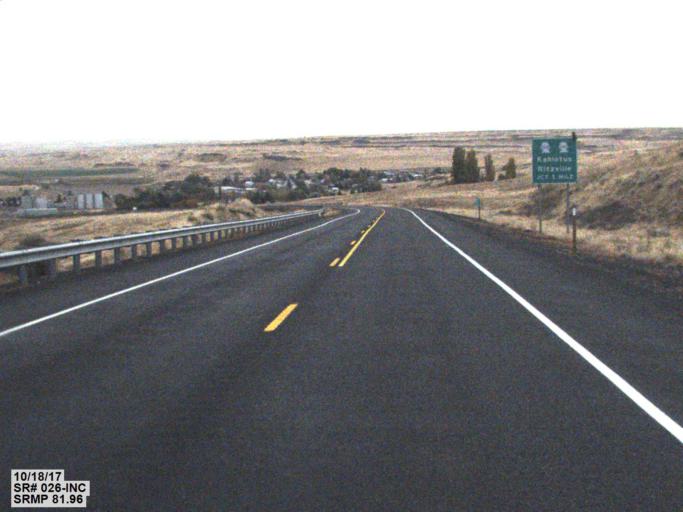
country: US
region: Washington
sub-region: Adams County
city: Ritzville
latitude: 46.7616
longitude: -118.3289
